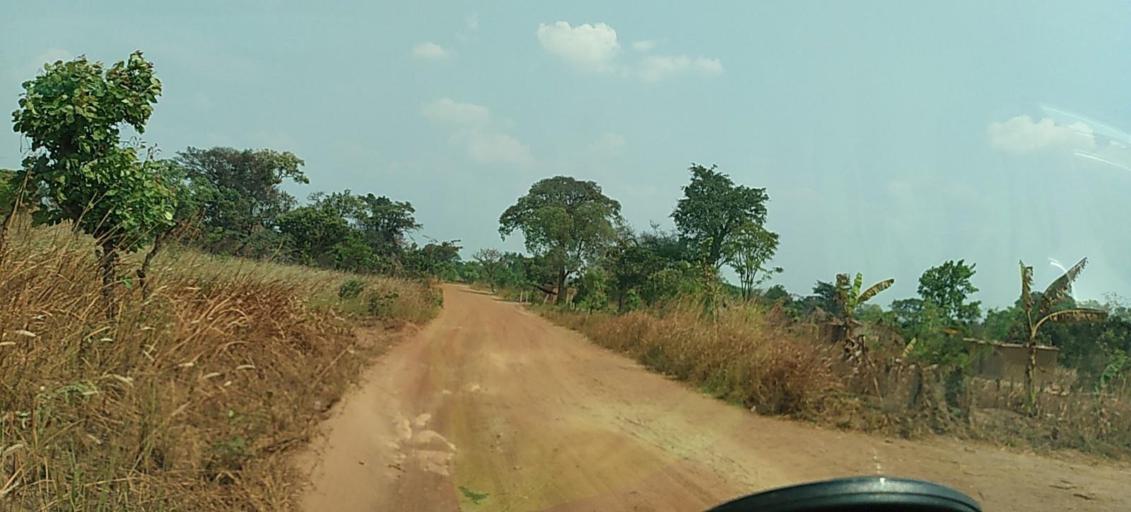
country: ZM
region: North-Western
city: Kansanshi
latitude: -12.1034
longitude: 26.3651
